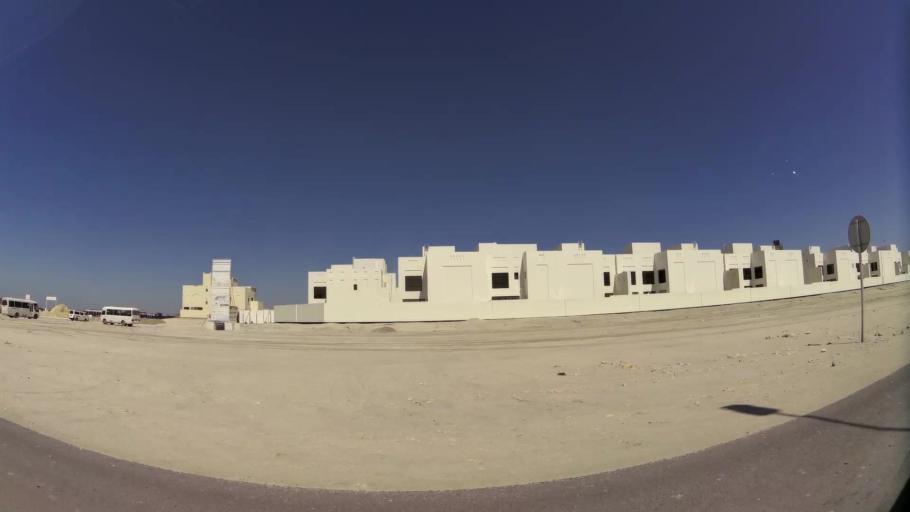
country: BH
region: Muharraq
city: Al Muharraq
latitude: 26.3001
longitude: 50.6320
